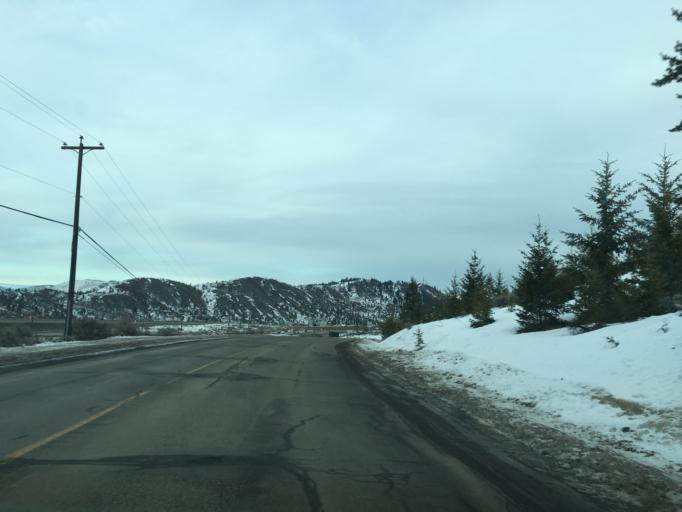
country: CA
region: British Columbia
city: Kamloops
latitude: 50.6635
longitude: -120.4317
